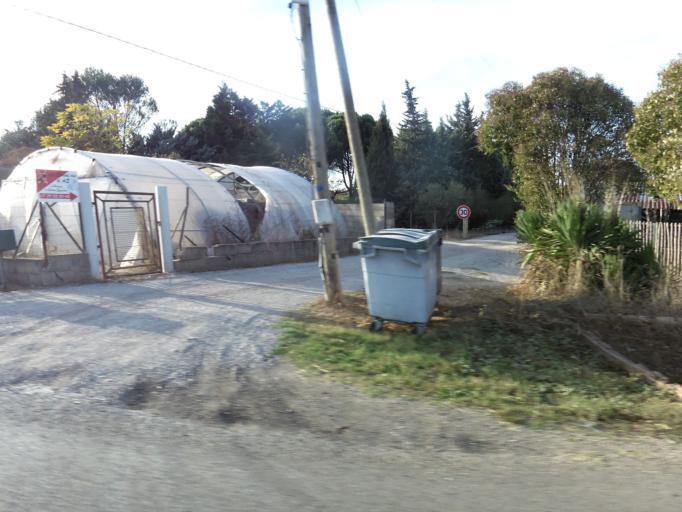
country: FR
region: Languedoc-Roussillon
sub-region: Departement du Gard
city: Aimargues
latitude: 43.7014
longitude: 4.2073
